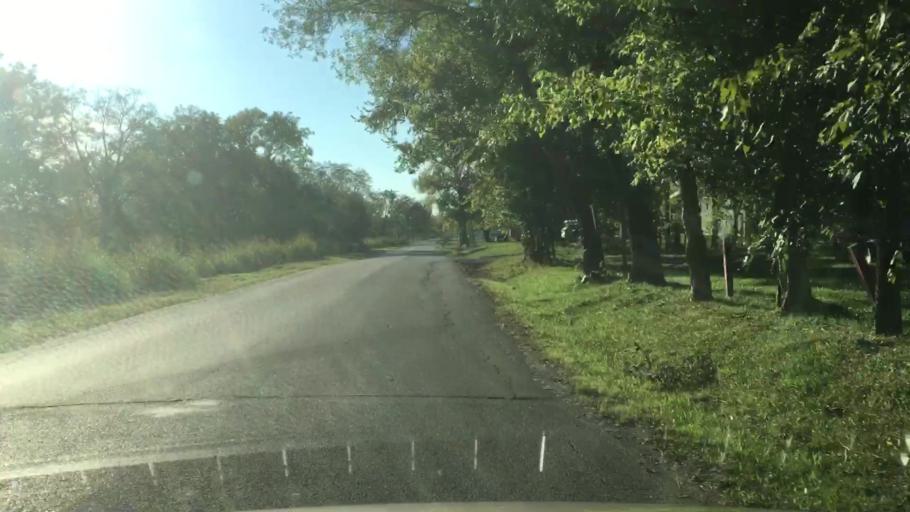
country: US
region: Oklahoma
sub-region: Muskogee County
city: Fort Gibson
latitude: 35.9297
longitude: -95.1415
